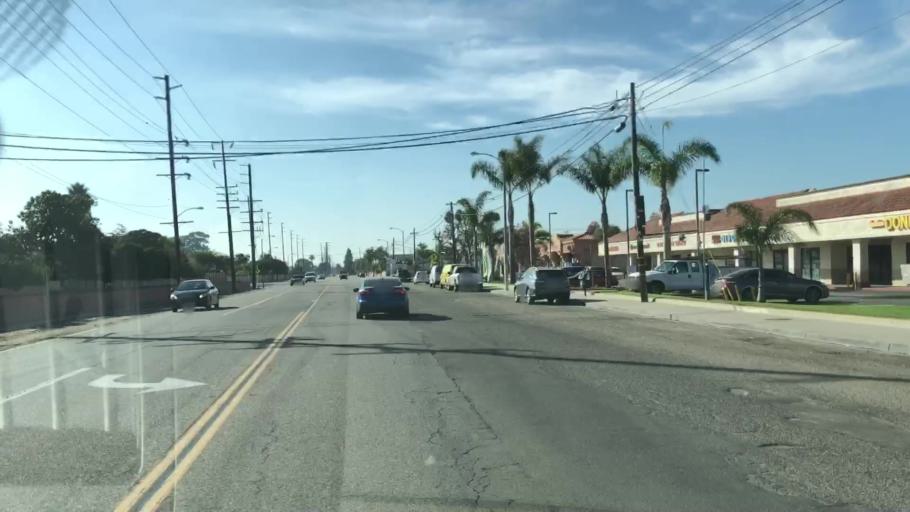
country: US
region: California
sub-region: Ventura County
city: Oxnard
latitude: 34.1733
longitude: -119.1494
